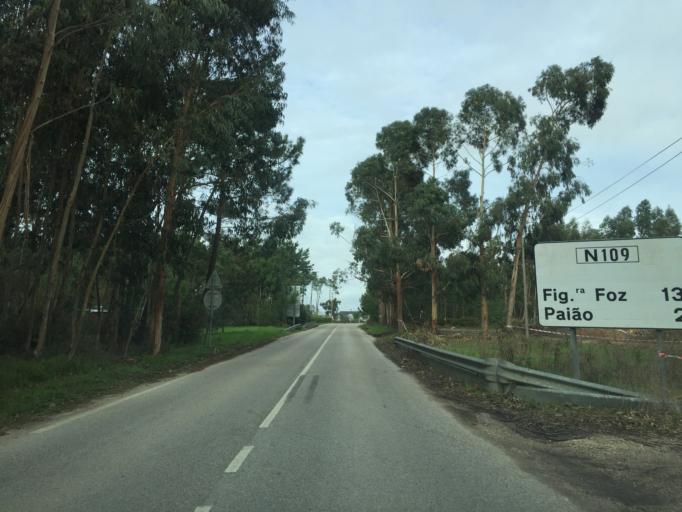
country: PT
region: Coimbra
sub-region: Figueira da Foz
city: Lavos
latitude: 40.0512
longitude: -8.8154
